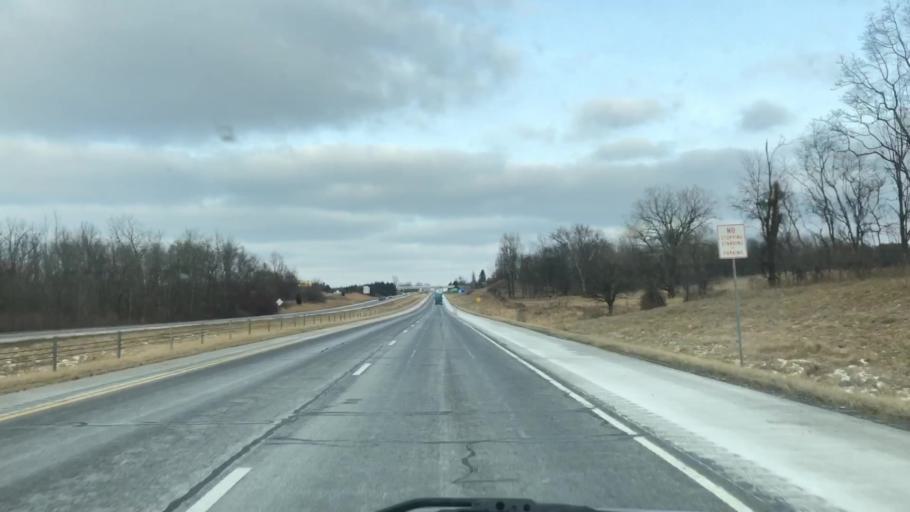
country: US
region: Indiana
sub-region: Steuben County
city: Angola
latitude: 41.6503
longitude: -85.0441
